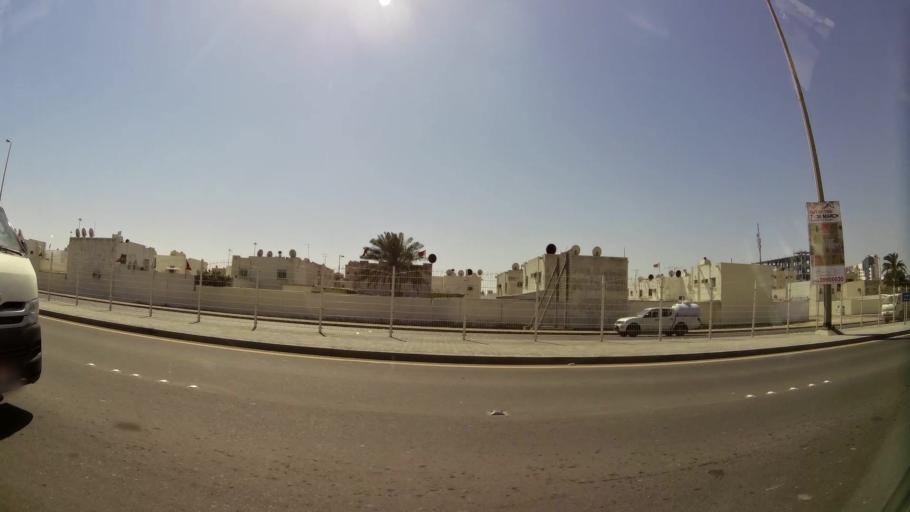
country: BH
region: Manama
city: Manama
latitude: 26.2015
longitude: 50.5896
